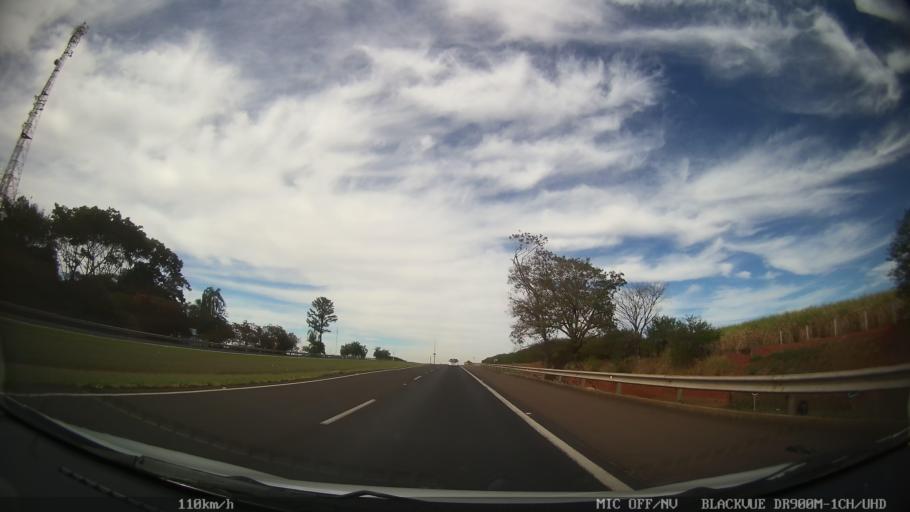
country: BR
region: Sao Paulo
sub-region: Taquaritinga
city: Taquaritinga
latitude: -21.5011
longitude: -48.5618
